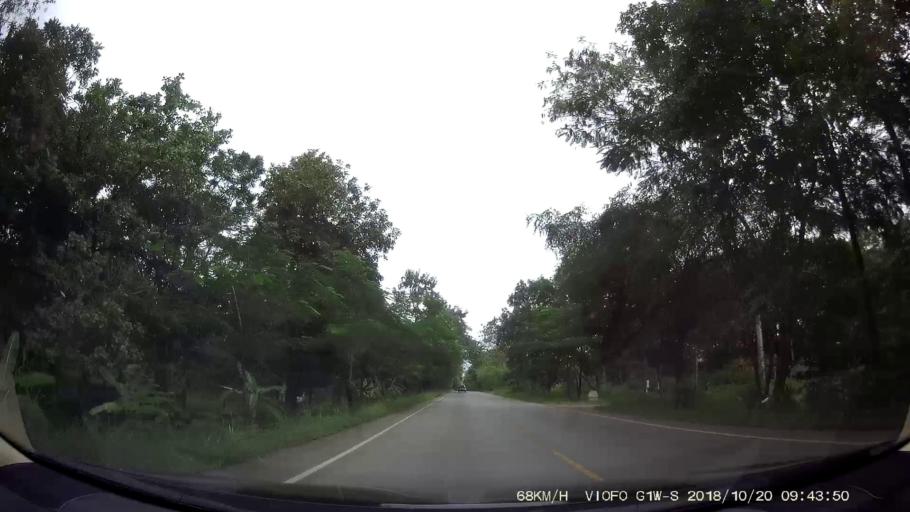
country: TH
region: Chaiyaphum
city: Khon San
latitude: 16.4772
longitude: 101.9465
